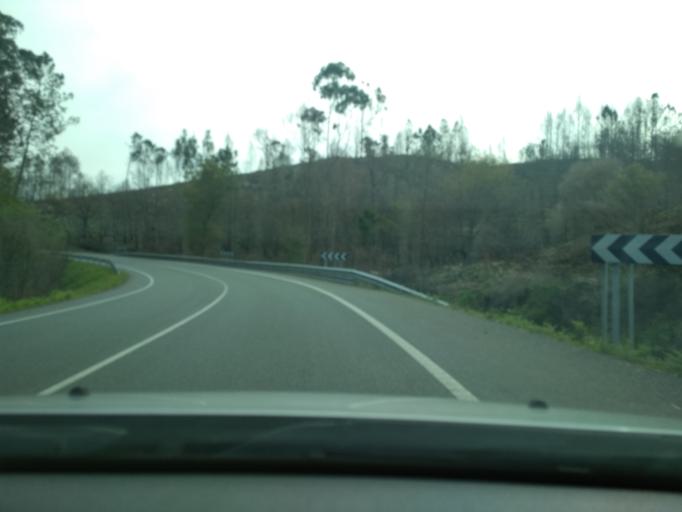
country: ES
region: Galicia
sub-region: Provincia de Pontevedra
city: Catoira
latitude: 42.6517
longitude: -8.6867
